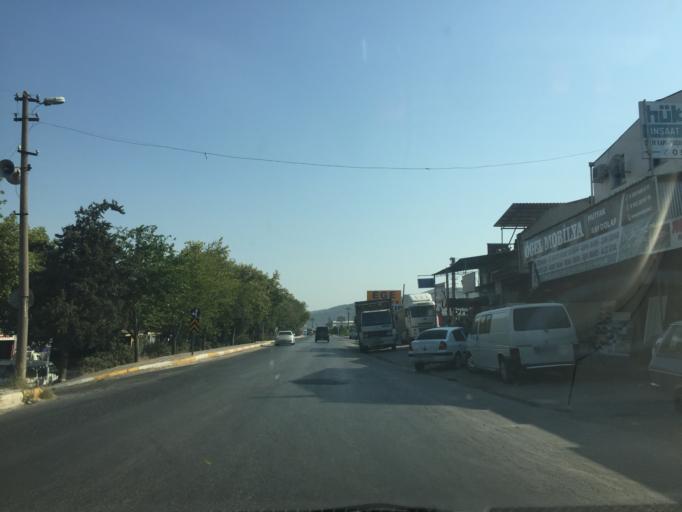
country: TR
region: Manisa
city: Akhisar
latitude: 38.9061
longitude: 27.8369
